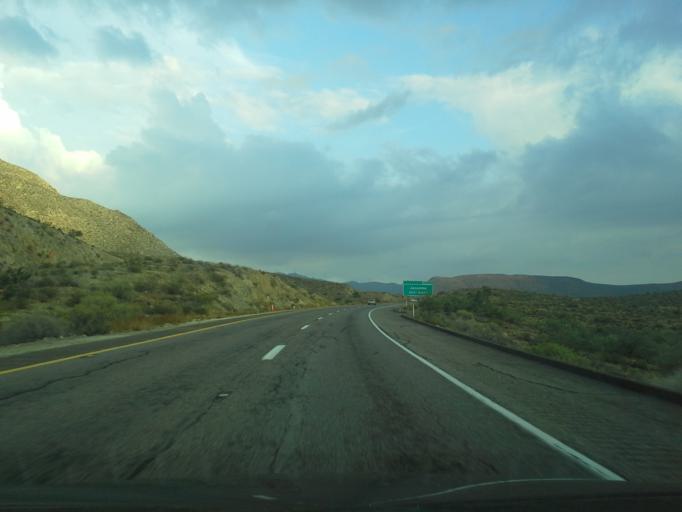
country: MX
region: Baja California
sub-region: Tecate
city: Cereso del Hongo
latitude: 32.6426
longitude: -116.1768
